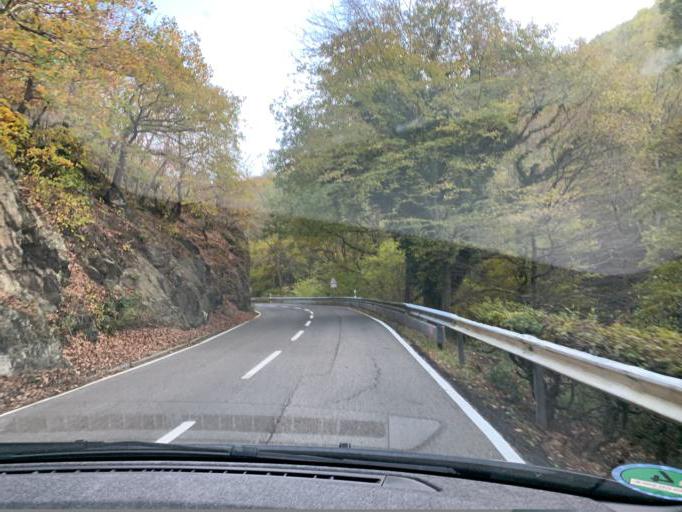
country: DE
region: North Rhine-Westphalia
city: Heimbach
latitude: 50.6281
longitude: 6.4817
